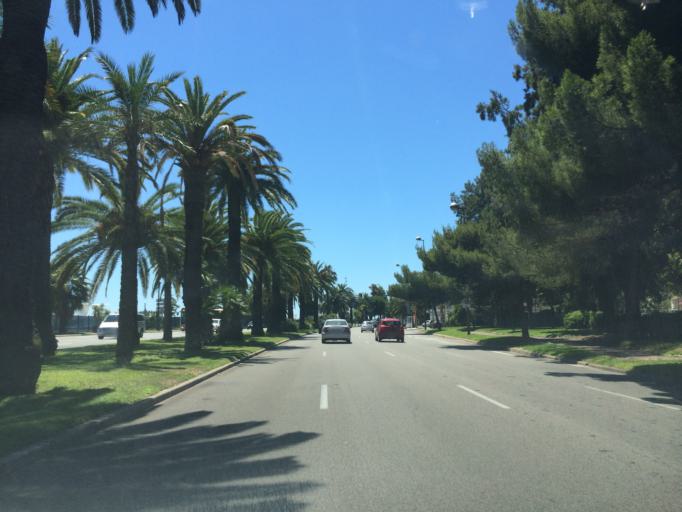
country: FR
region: Provence-Alpes-Cote d'Azur
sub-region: Departement des Alpes-Maritimes
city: Nice
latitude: 43.6741
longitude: 7.2269
